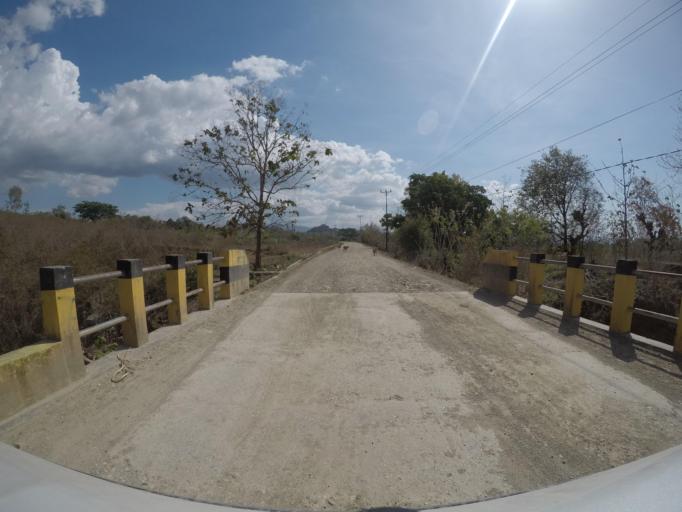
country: TL
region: Bobonaro
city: Maliana
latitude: -8.9954
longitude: 125.2008
